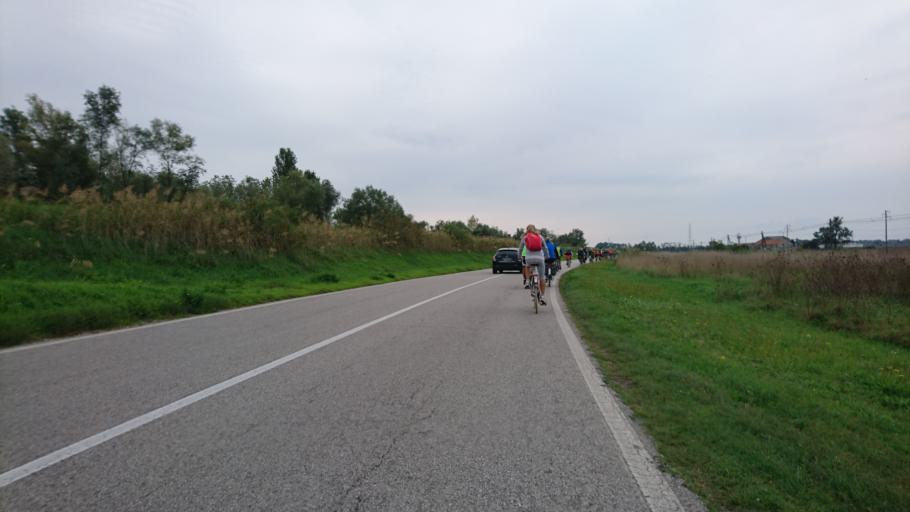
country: IT
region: Veneto
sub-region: Provincia di Rovigo
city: Scardovari
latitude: 44.9529
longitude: 12.4192
